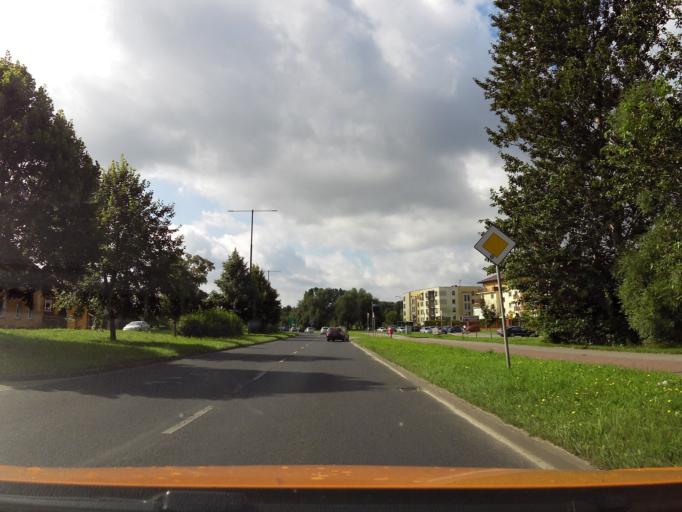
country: PL
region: West Pomeranian Voivodeship
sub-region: Powiat kolobrzeski
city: Kolobrzeg
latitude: 54.1651
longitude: 15.5678
